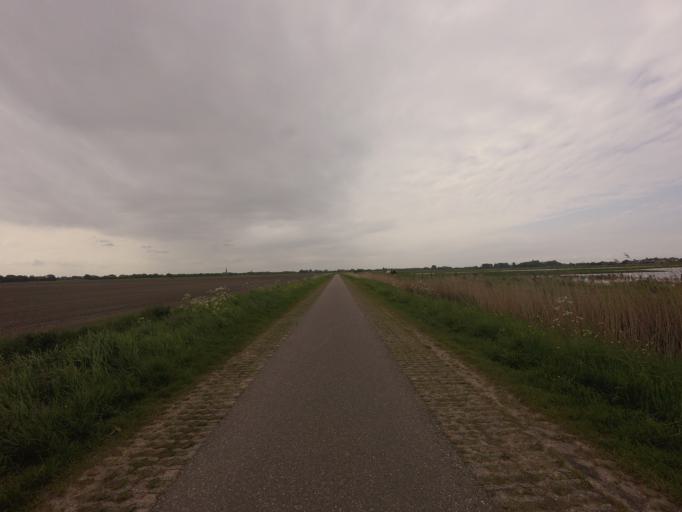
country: NL
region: Zeeland
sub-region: Gemeente Middelburg
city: Middelburg
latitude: 51.5236
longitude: 3.5867
